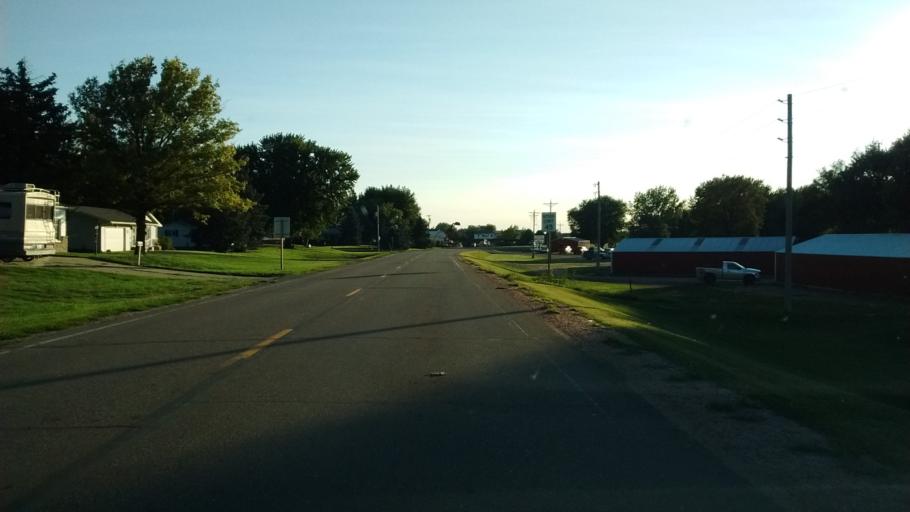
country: US
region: Iowa
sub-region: Plymouth County
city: Kingsley
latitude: 42.5843
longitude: -95.9683
